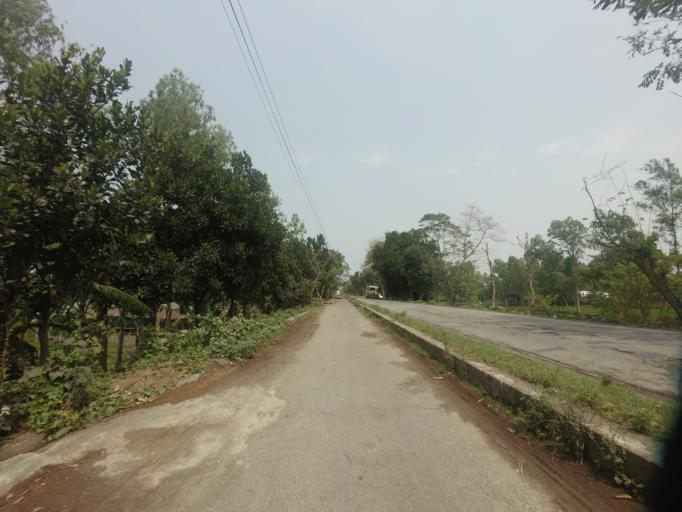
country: BD
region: Rajshahi
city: Sirajganj
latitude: 24.3544
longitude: 89.7038
